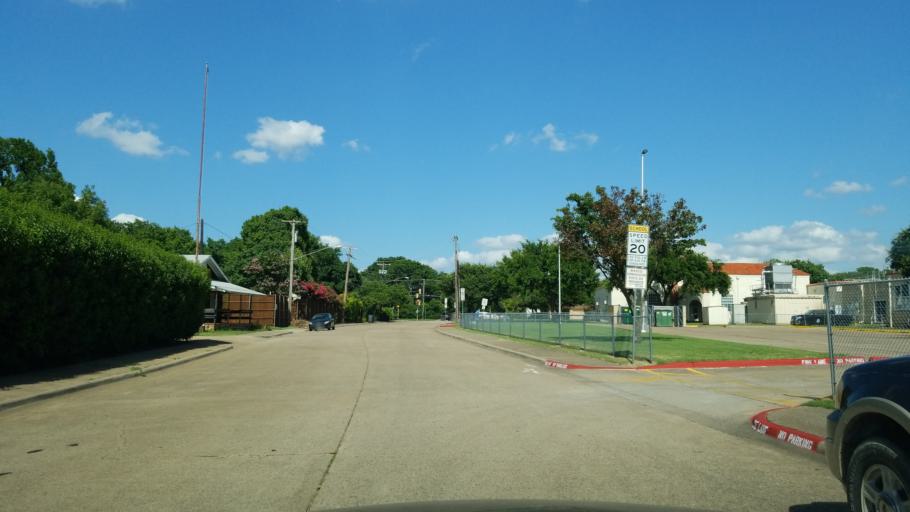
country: US
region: Texas
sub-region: Dallas County
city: University Park
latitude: 32.8836
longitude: -96.8403
